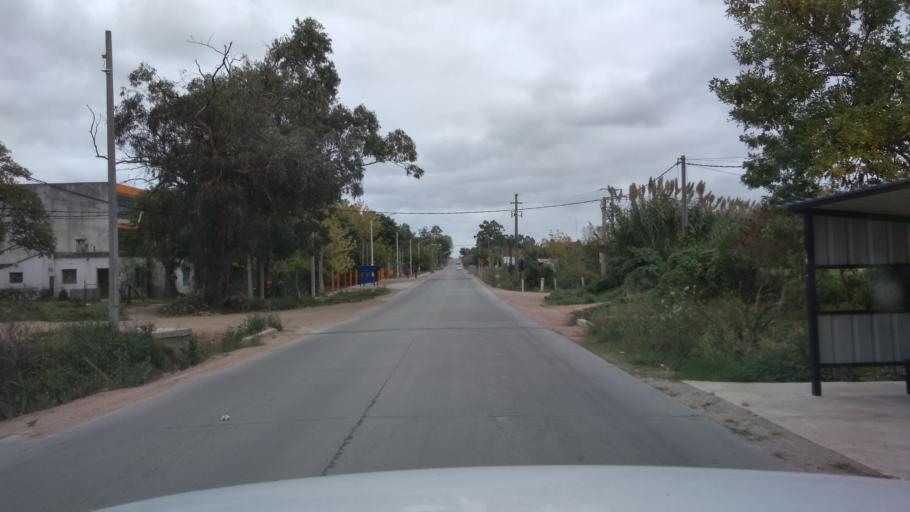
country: UY
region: Canelones
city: Toledo
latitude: -34.7831
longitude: -56.1384
